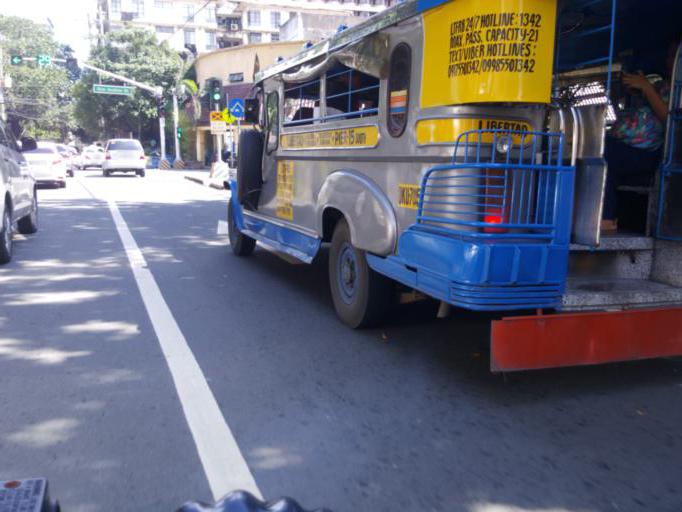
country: PH
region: Metro Manila
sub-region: City of Manila
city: Port Area
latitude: 14.5691
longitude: 120.9843
